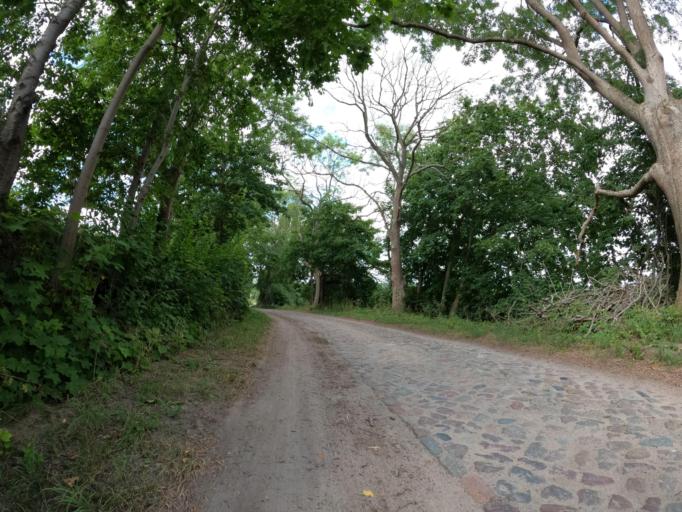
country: DE
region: Mecklenburg-Vorpommern
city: Woldegk
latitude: 53.4079
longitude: 13.6214
